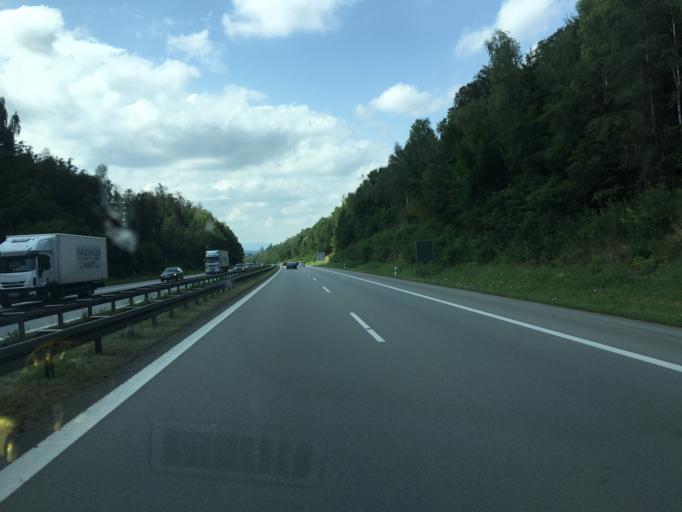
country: DE
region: Bavaria
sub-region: Lower Bavaria
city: Passau
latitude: 48.5501
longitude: 13.3960
